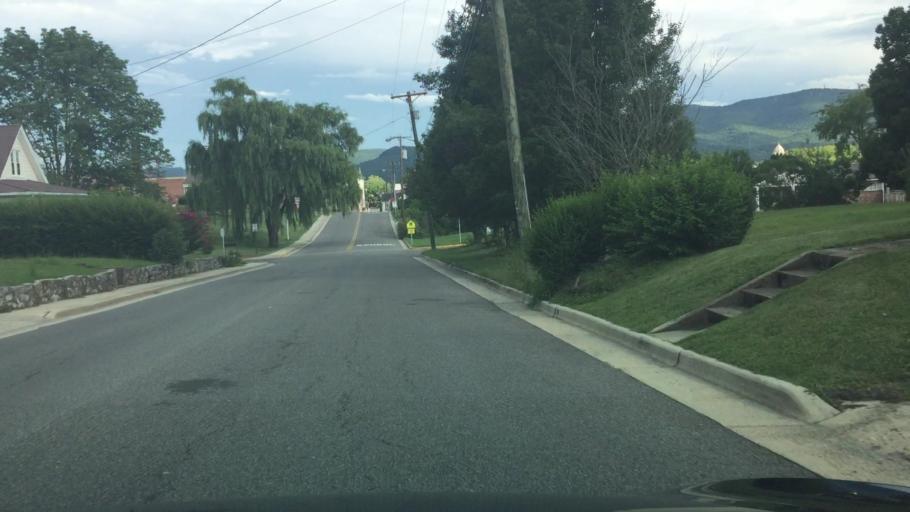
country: US
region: Virginia
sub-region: Wythe County
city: Wytheville
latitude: 36.9530
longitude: -81.0872
